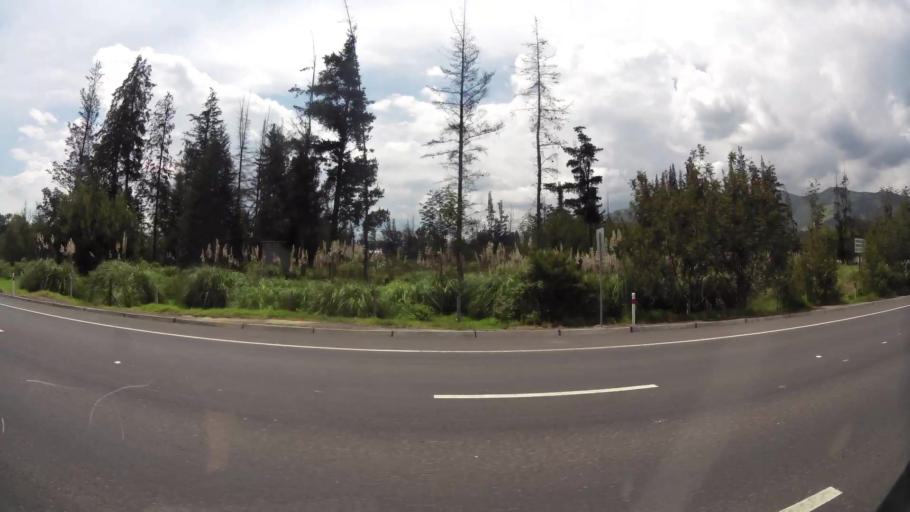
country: EC
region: Pichincha
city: Sangolqui
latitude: -0.2033
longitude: -78.3344
